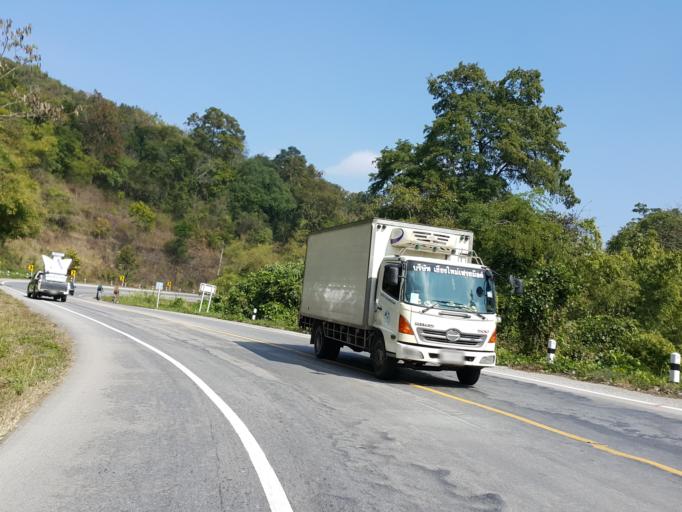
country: TH
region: Lampang
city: Wang Nuea
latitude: 19.0929
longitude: 99.4231
